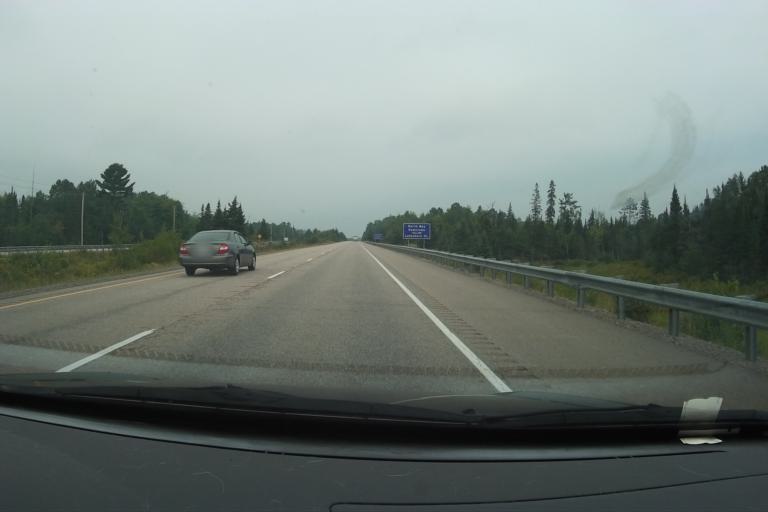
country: CA
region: Ontario
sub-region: Nipissing District
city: North Bay
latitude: 46.2451
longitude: -79.3624
